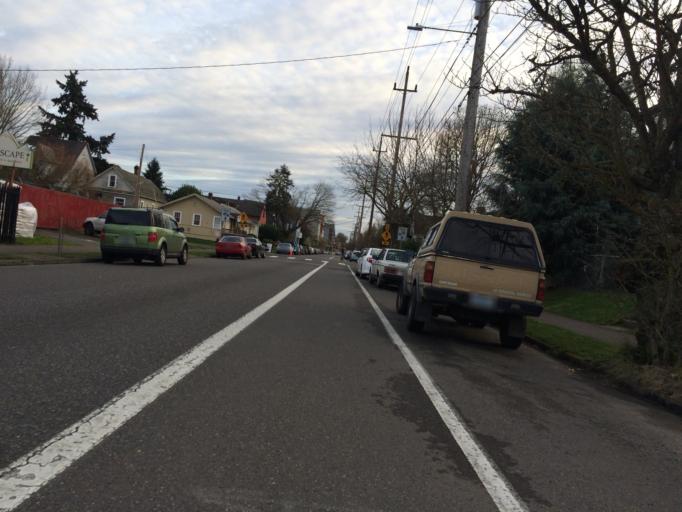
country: US
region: Oregon
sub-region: Multnomah County
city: Portland
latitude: 45.5514
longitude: -122.6680
